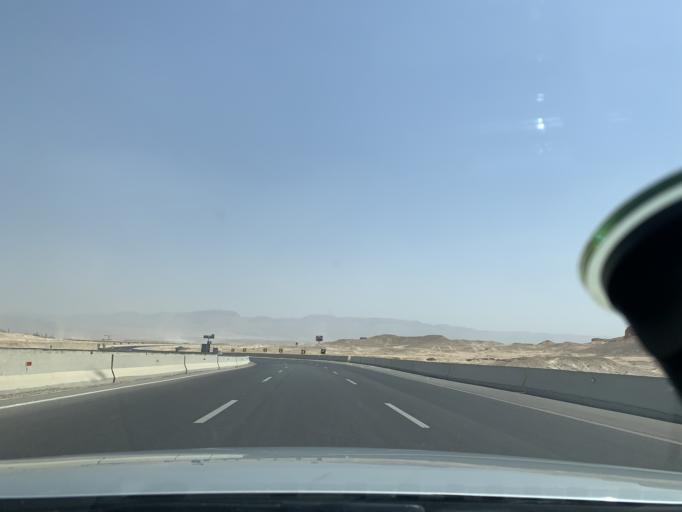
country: EG
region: As Suways
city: Ain Sukhna
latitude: 29.6689
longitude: 32.2334
